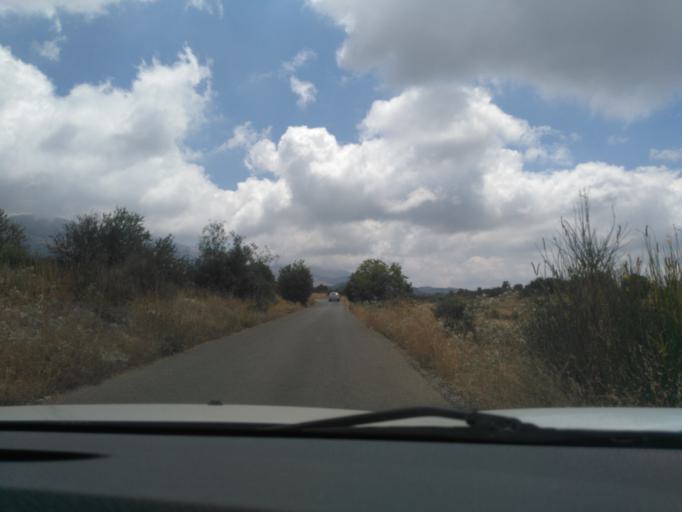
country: LB
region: Mont-Liban
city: Beit ed Dine
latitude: 33.6802
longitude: 35.6638
